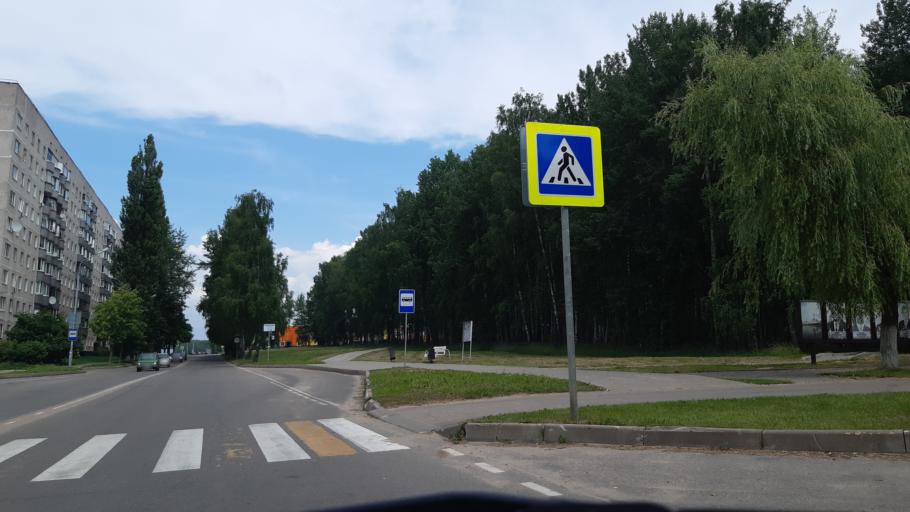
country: RU
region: Smolensk
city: Desnogorsk
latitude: 54.1563
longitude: 33.2907
